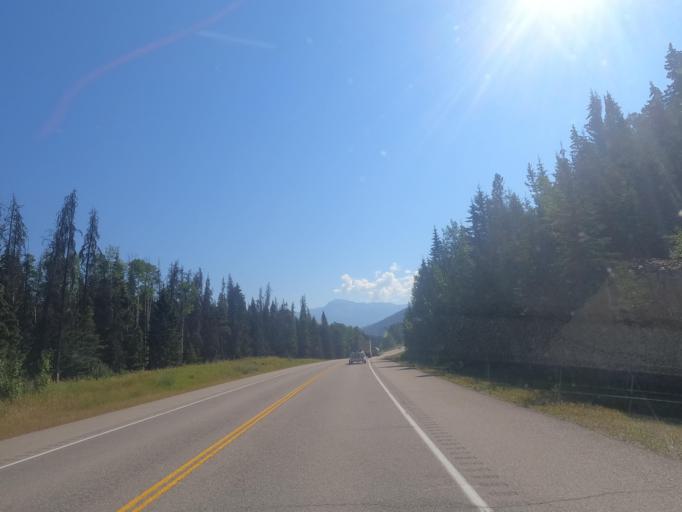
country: CA
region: Alberta
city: Jasper Park Lodge
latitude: 52.8603
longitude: -118.1787
